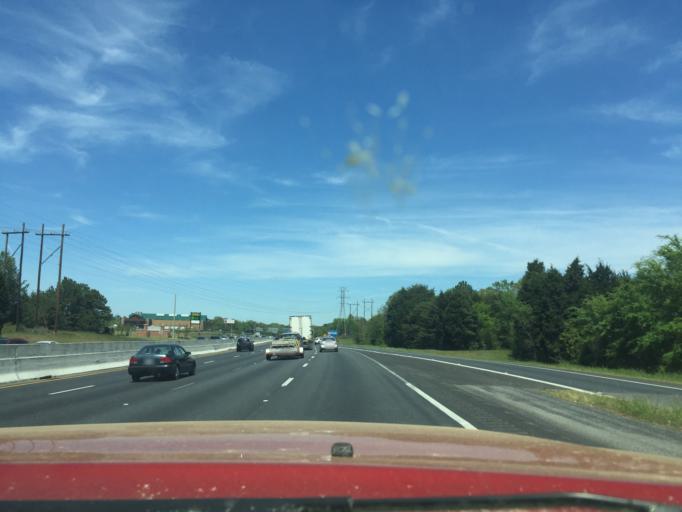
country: US
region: North Carolina
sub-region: Mecklenburg County
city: Pineville
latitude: 35.0940
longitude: -80.9325
